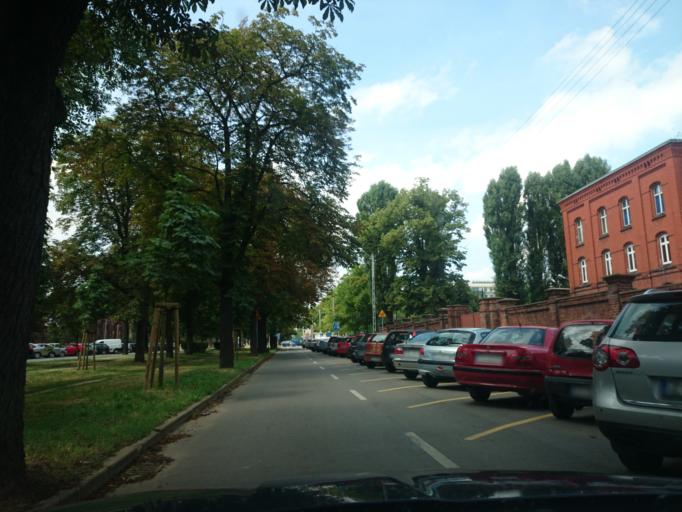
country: PL
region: West Pomeranian Voivodeship
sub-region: Szczecin
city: Szczecin
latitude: 53.4213
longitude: 14.5435
